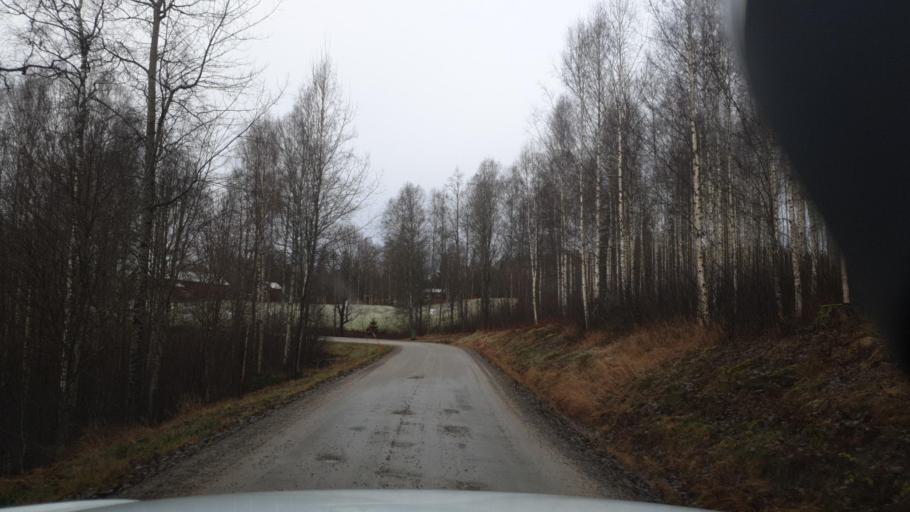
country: SE
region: Vaermland
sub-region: Arvika Kommun
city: Arvika
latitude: 59.7149
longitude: 12.8464
